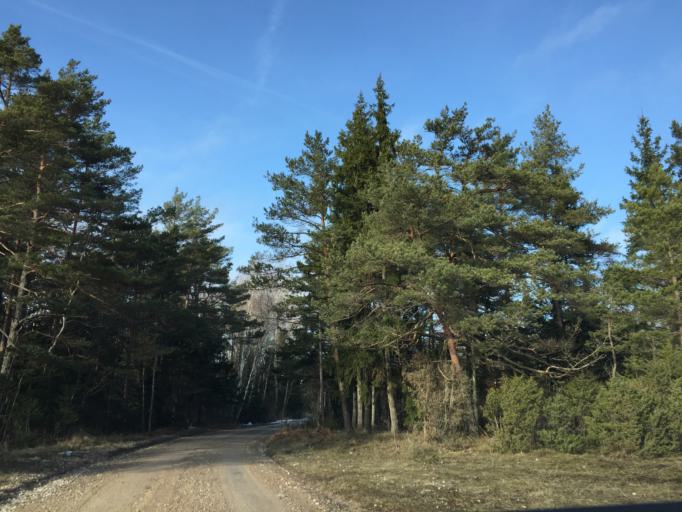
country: EE
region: Saare
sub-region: Kuressaare linn
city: Kuressaare
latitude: 58.4776
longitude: 21.9518
